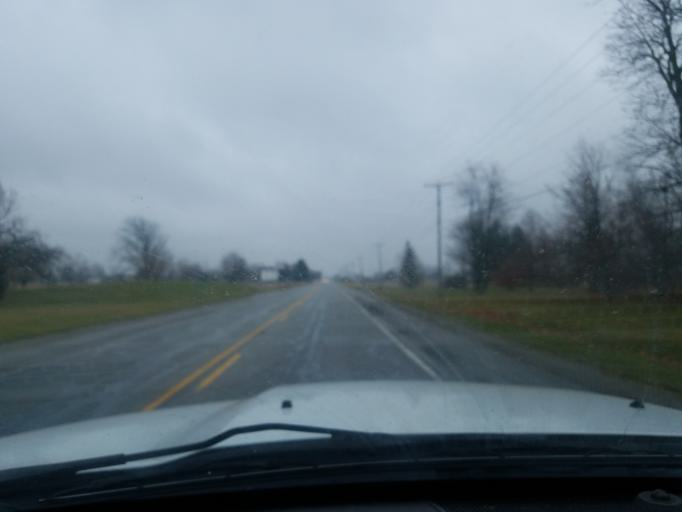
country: US
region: Indiana
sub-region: Wells County
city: Ossian
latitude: 40.9431
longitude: -85.1676
